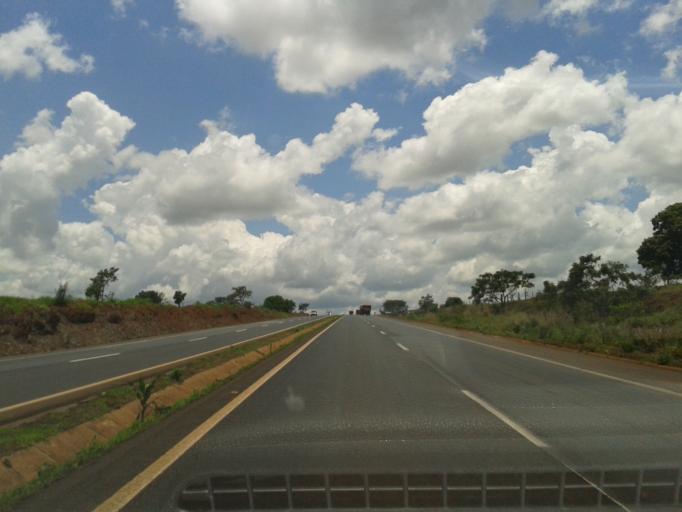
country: BR
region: Minas Gerais
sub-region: Centralina
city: Centralina
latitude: -18.6653
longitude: -49.1643
